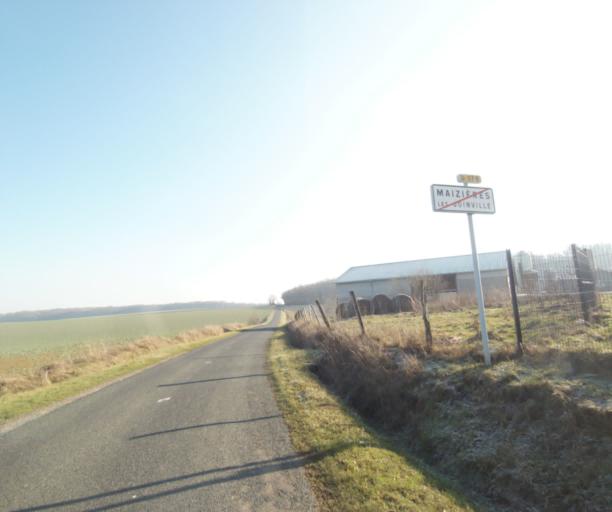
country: FR
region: Champagne-Ardenne
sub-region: Departement de la Haute-Marne
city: Chevillon
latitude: 48.4920
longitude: 5.0734
